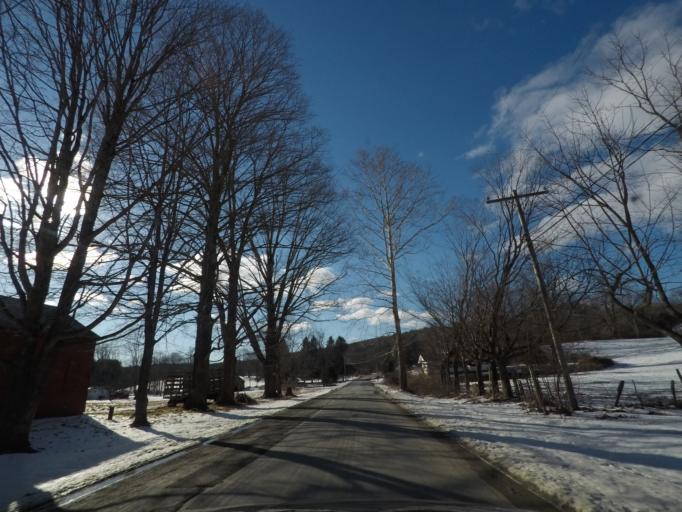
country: US
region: New York
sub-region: Rensselaer County
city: Nassau
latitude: 42.5161
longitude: -73.5165
